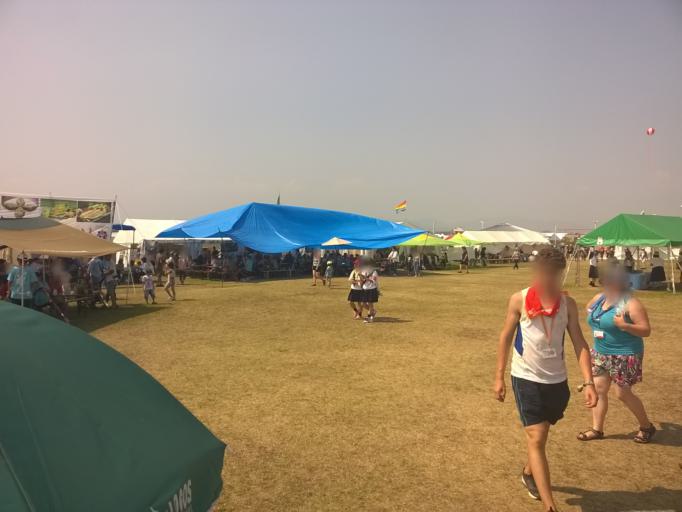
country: JP
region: Yamaguchi
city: Ogori-shimogo
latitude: 34.0063
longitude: 131.3701
